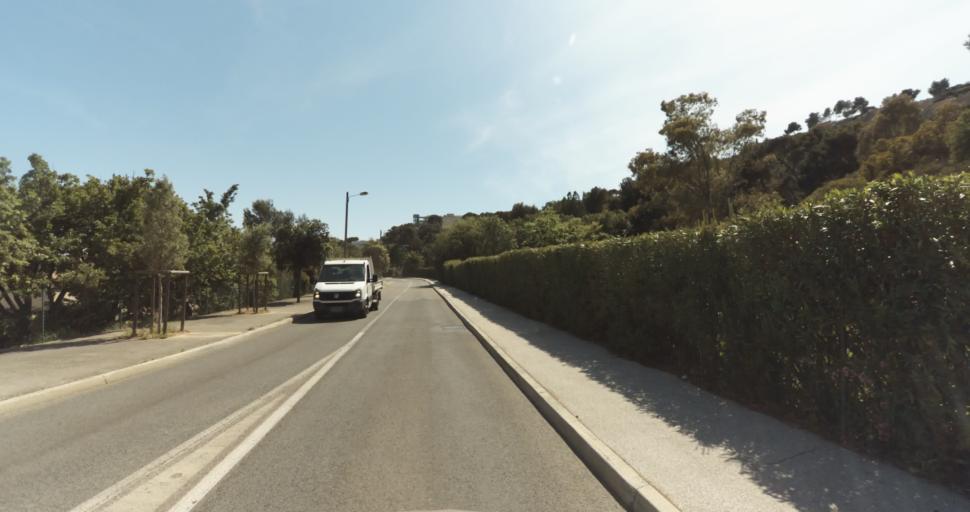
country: FR
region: Provence-Alpes-Cote d'Azur
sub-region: Departement du Var
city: Hyeres
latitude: 43.0904
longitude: 6.1222
